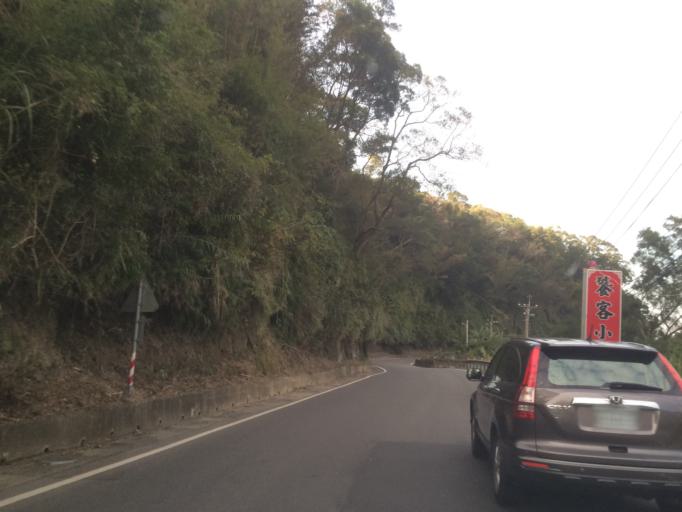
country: TW
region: Taiwan
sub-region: Hsinchu
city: Hsinchu
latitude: 24.6980
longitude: 121.0957
